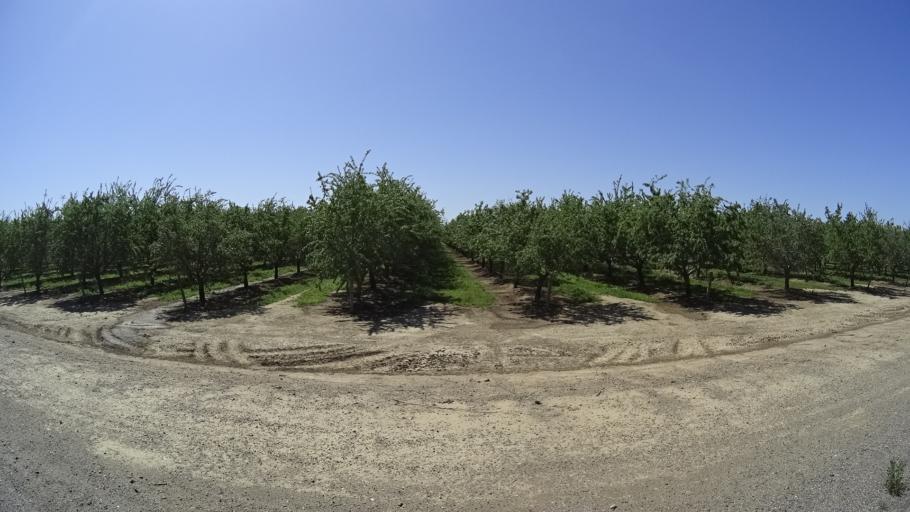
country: US
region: California
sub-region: Glenn County
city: Orland
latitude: 39.6961
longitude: -122.1323
